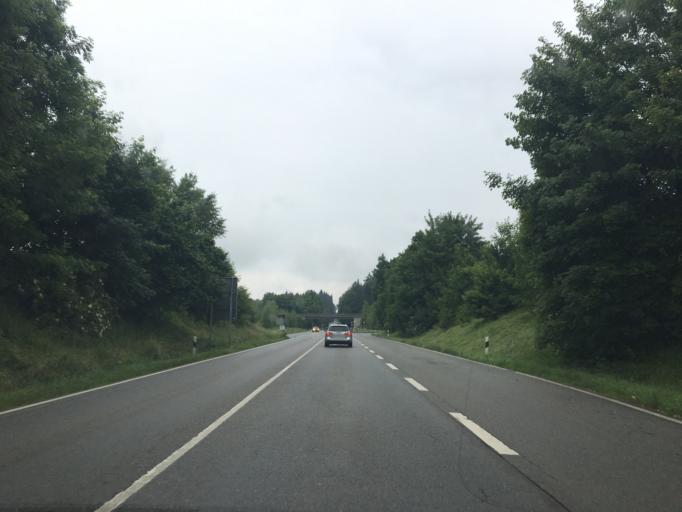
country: DE
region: Bavaria
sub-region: Upper Bavaria
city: Holzkirchen
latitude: 47.8780
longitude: 11.7193
